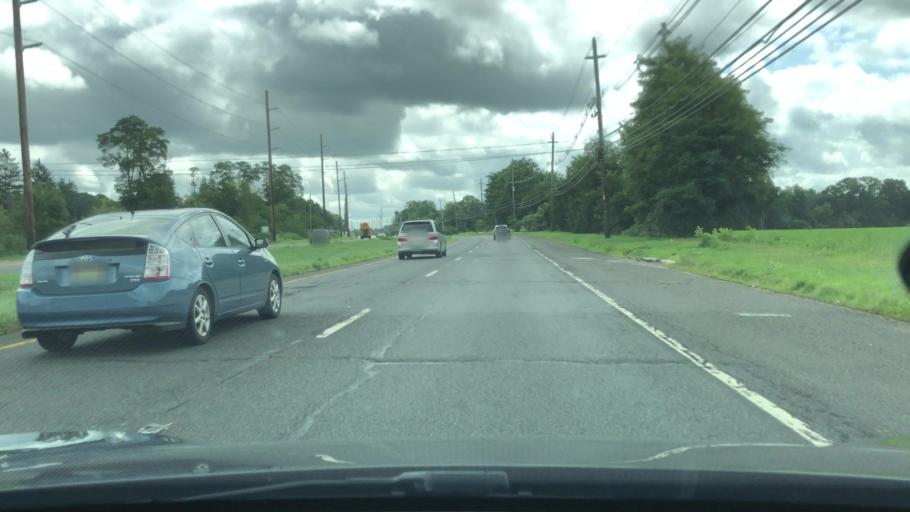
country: US
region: New Jersey
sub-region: Mercer County
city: Twin Rivers
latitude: 40.2642
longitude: -74.4519
